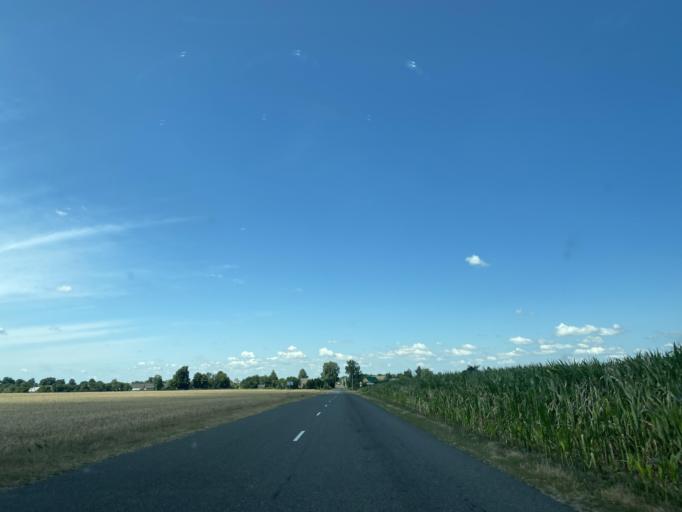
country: BY
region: Brest
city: Ivanava
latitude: 52.1732
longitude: 25.5666
